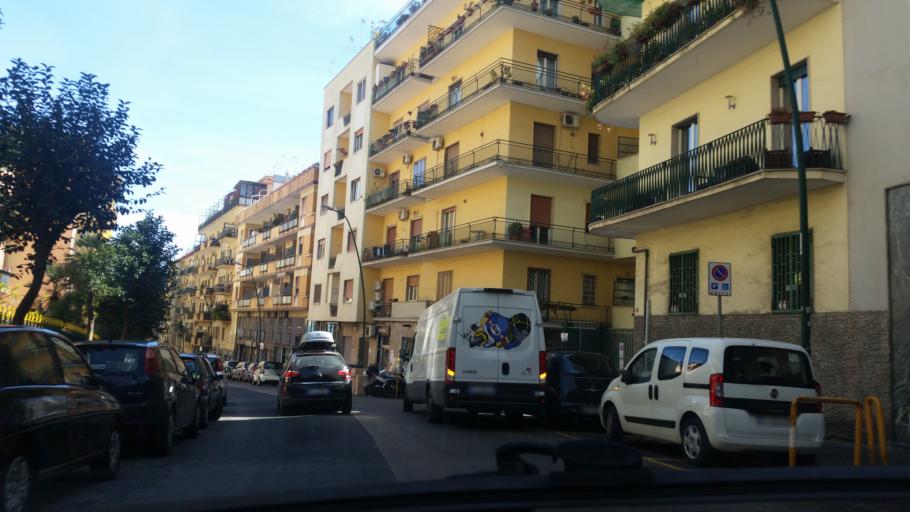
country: IT
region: Campania
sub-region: Provincia di Napoli
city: Napoli
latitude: 40.8526
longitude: 14.2363
